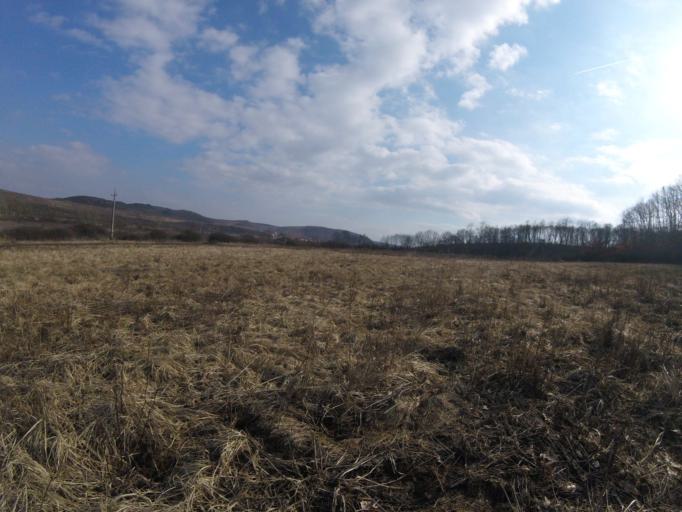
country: HU
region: Heves
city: Egerszalok
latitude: 47.8459
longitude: 20.3251
